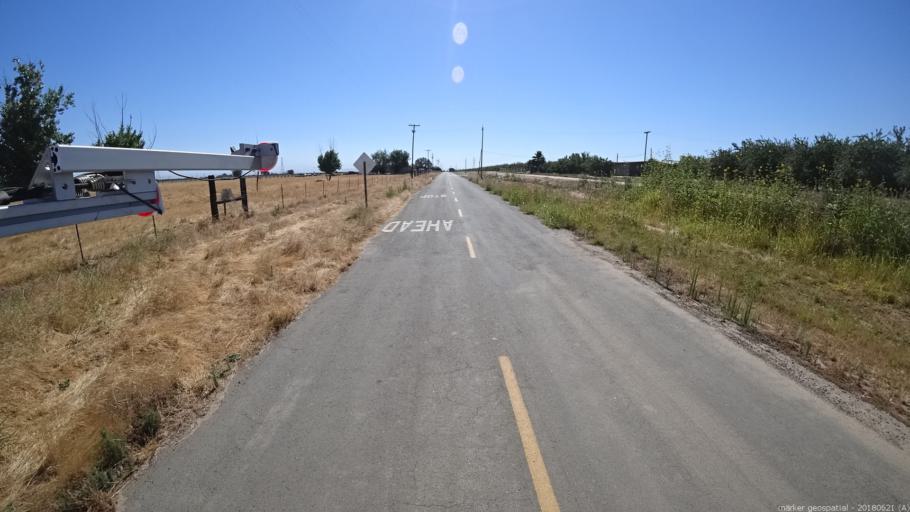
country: US
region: California
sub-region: Fresno County
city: Biola
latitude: 36.8658
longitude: -119.9451
